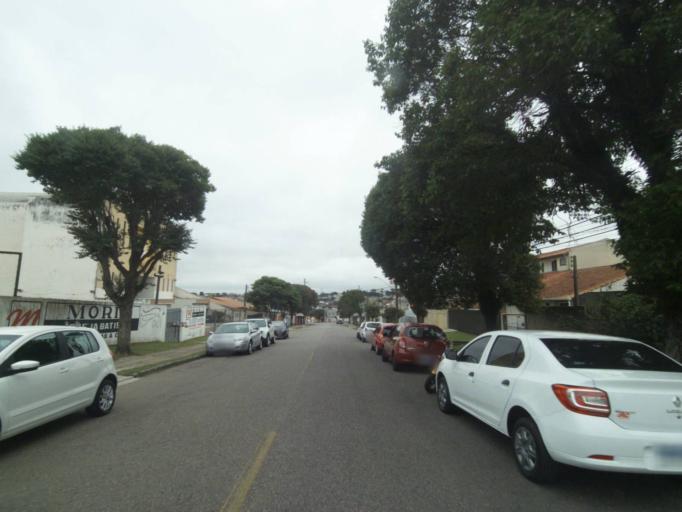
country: BR
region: Parana
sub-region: Sao Jose Dos Pinhais
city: Sao Jose dos Pinhais
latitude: -25.5380
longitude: -49.2817
